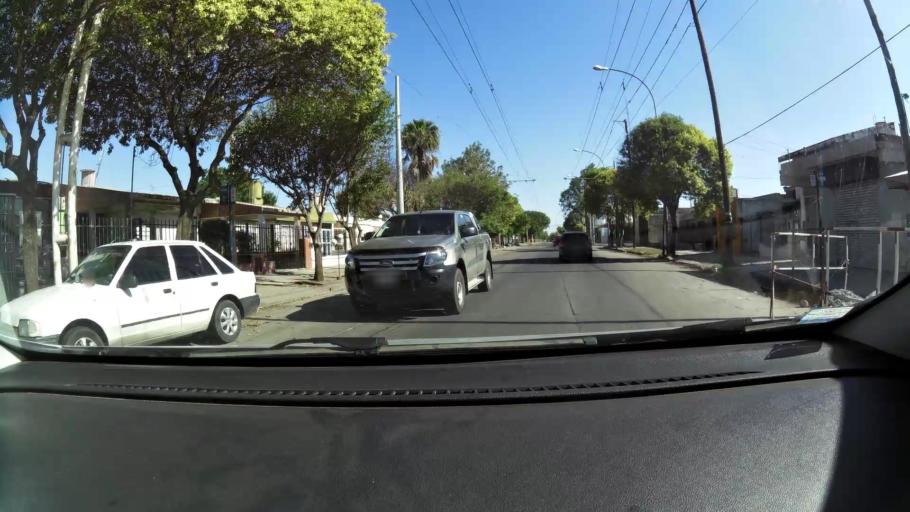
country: AR
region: Cordoba
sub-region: Departamento de Capital
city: Cordoba
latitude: -31.3745
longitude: -64.1838
